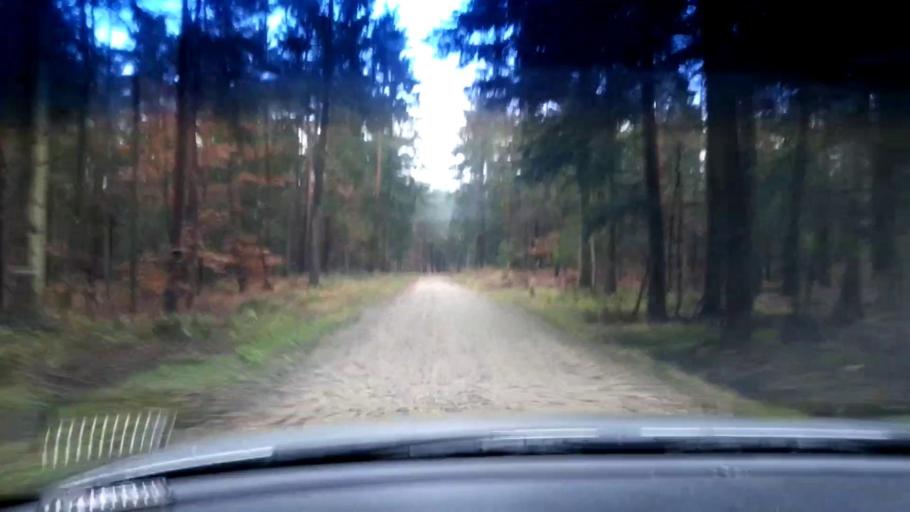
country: DE
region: Bavaria
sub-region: Upper Franconia
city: Kemmern
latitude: 49.9569
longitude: 10.8958
